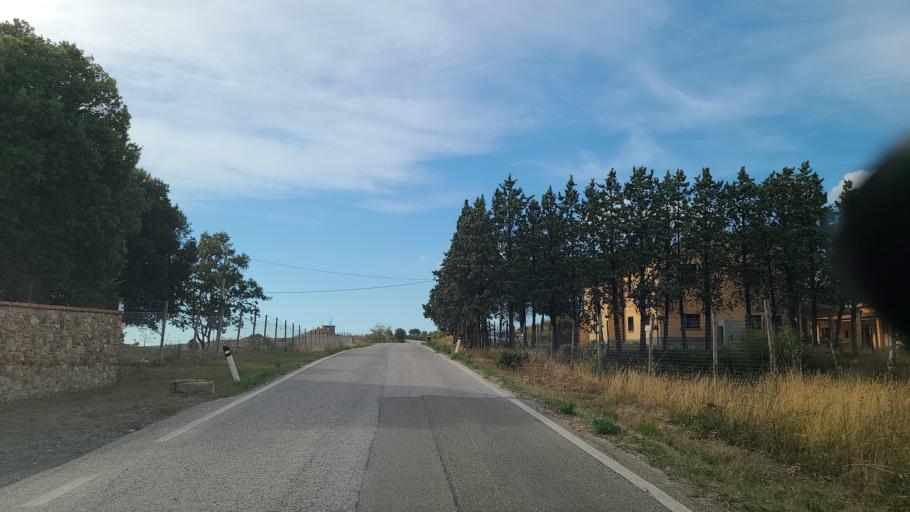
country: IT
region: Tuscany
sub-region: Provincia di Siena
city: San Gimignano
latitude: 43.4398
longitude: 10.9586
